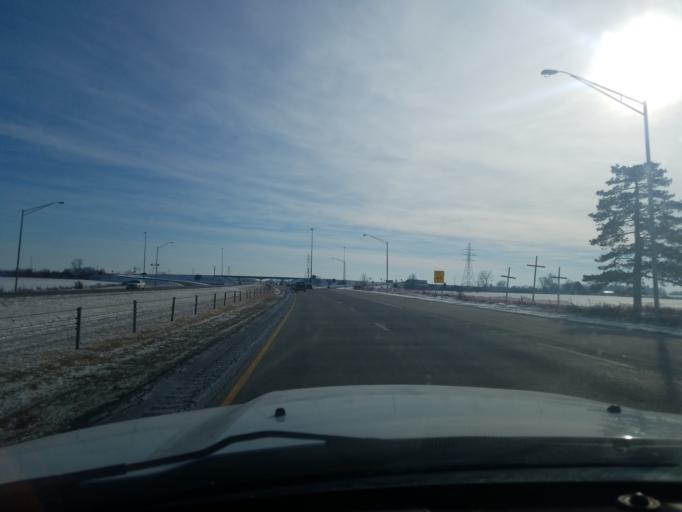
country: US
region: Indiana
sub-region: Grant County
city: Upland
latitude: 40.4273
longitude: -85.5495
